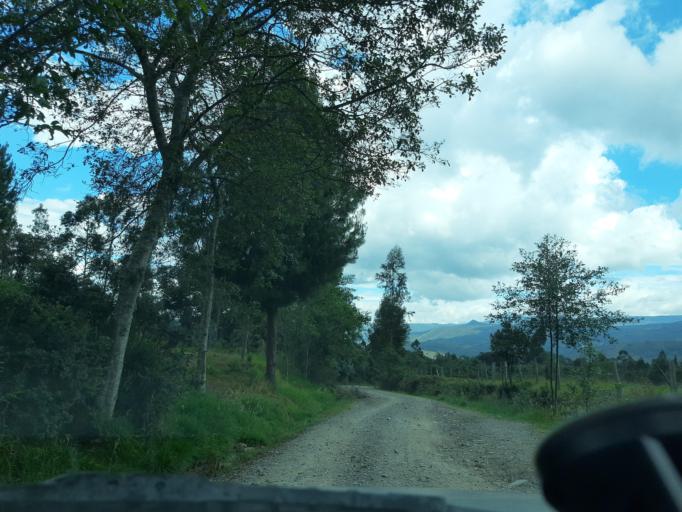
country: CO
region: Boyaca
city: Raquira
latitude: 5.5078
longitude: -73.6803
